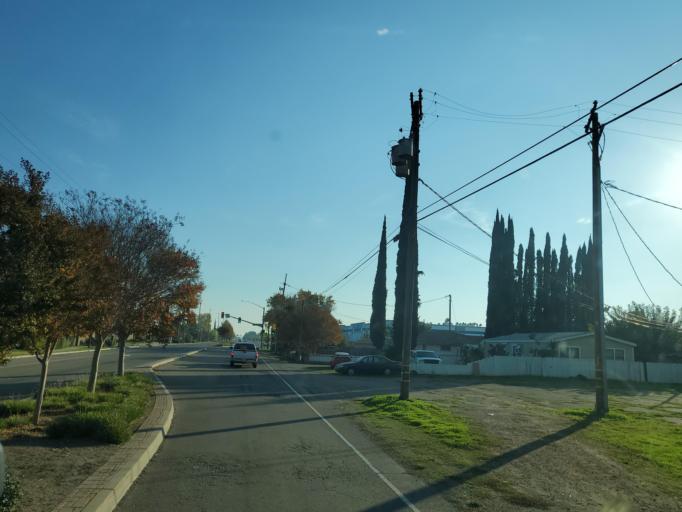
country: US
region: California
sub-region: San Joaquin County
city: Lathrop
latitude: 37.8331
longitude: -121.2542
